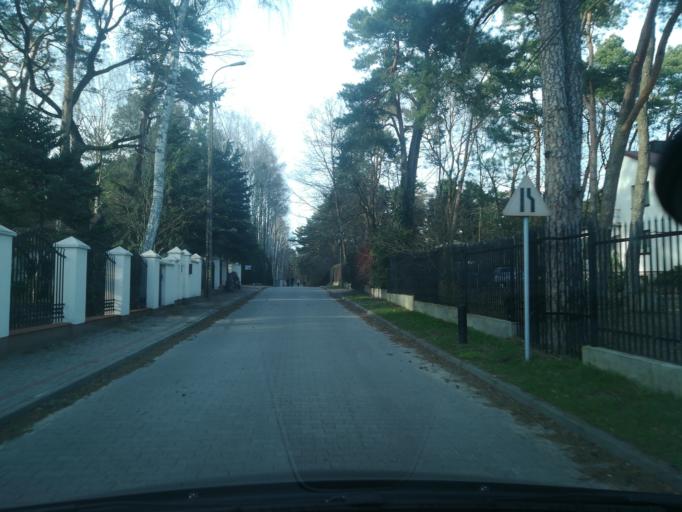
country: PL
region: Masovian Voivodeship
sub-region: Powiat piaseczynski
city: Konstancin-Jeziorna
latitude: 52.0717
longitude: 21.1047
